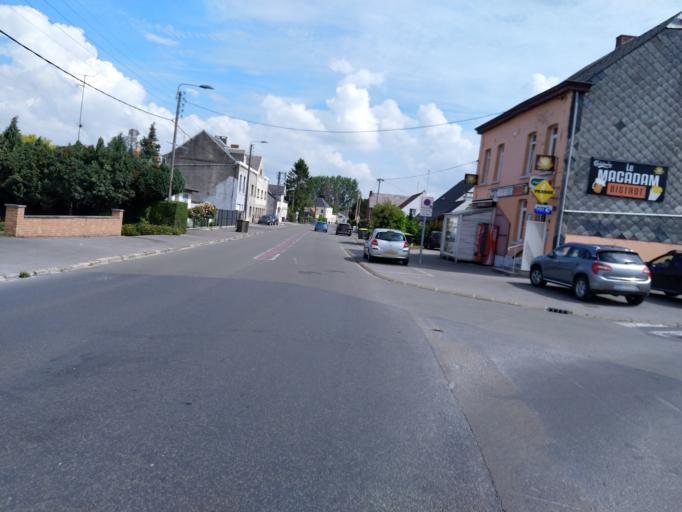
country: FR
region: Nord-Pas-de-Calais
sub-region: Departement du Nord
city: Maubeuge
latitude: 50.2864
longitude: 3.9839
